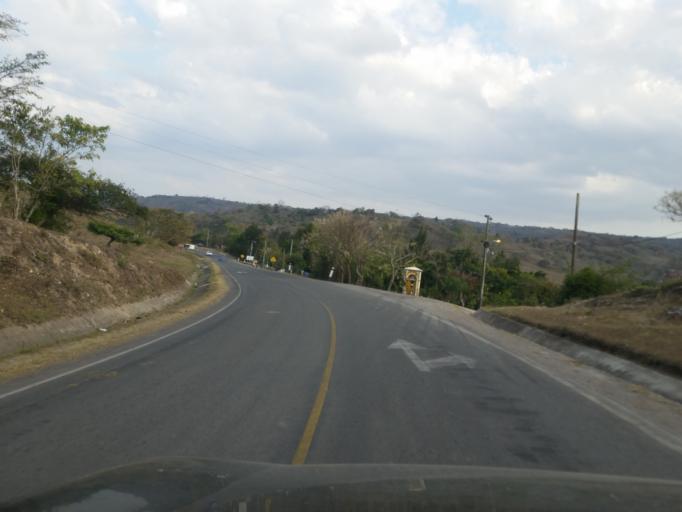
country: NI
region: Jinotega
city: San Rafael del Norte
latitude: 13.1925
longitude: -86.1106
